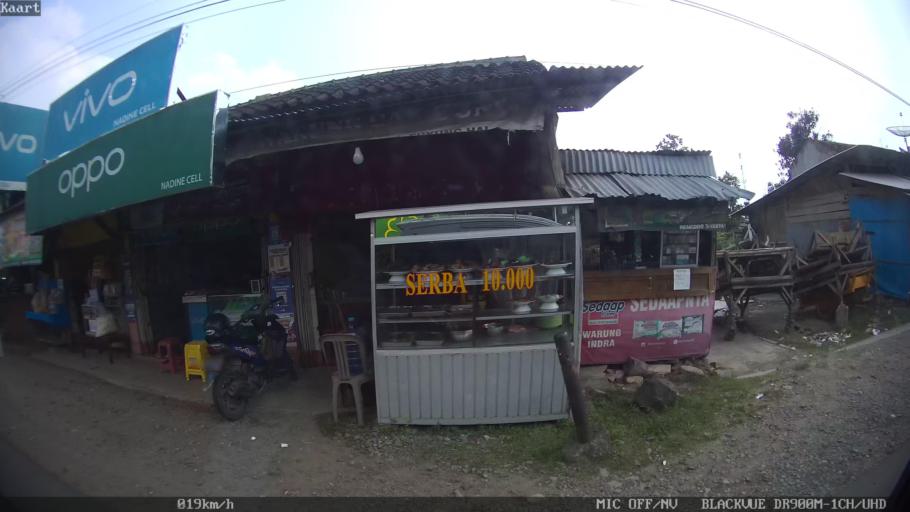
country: ID
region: Lampung
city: Gadingrejo
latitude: -5.3735
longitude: 105.0598
